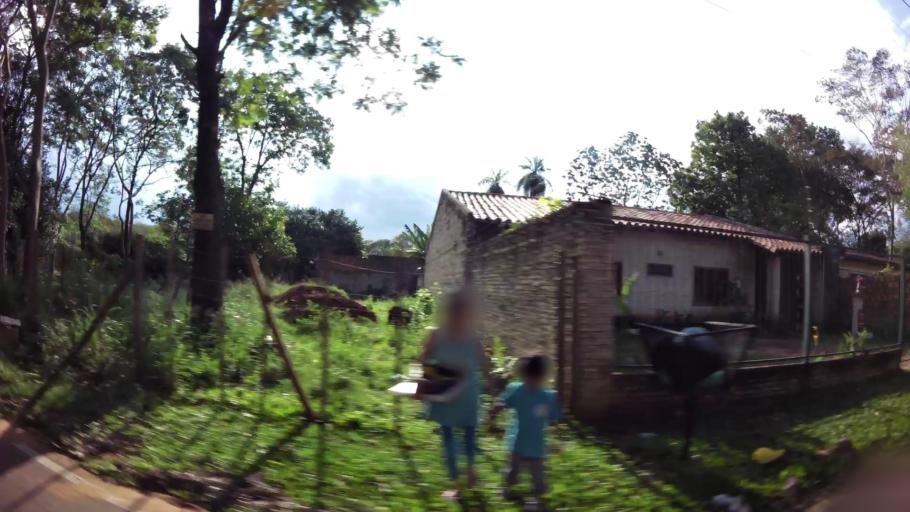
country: PY
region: Central
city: Fernando de la Mora
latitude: -25.3490
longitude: -57.5528
